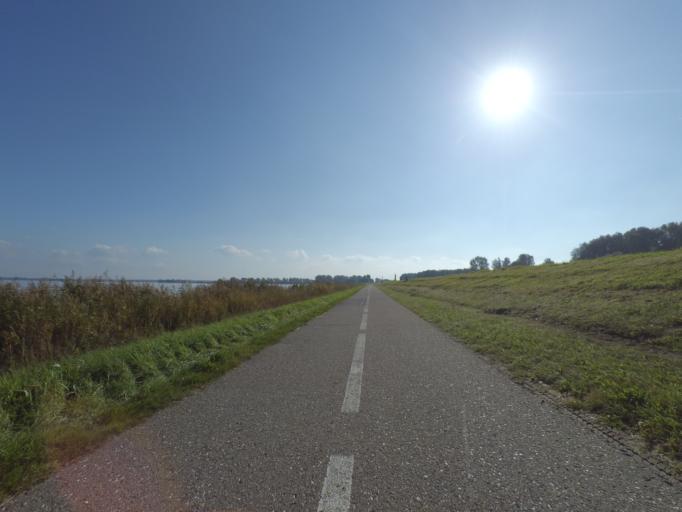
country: NL
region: Flevoland
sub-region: Gemeente Zeewolde
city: Zeewolde
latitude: 52.3406
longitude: 5.5399
